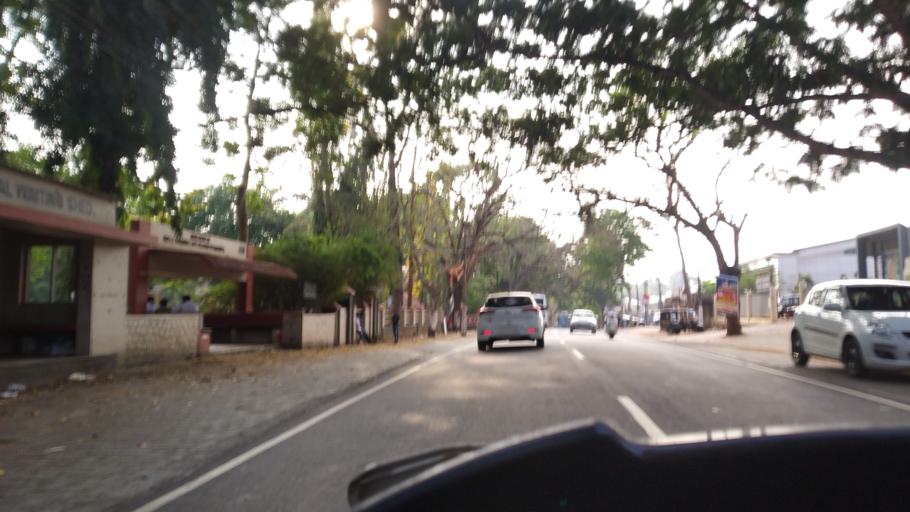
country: IN
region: Kerala
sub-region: Kottayam
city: Erattupetta
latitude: 9.5697
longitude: 76.8183
